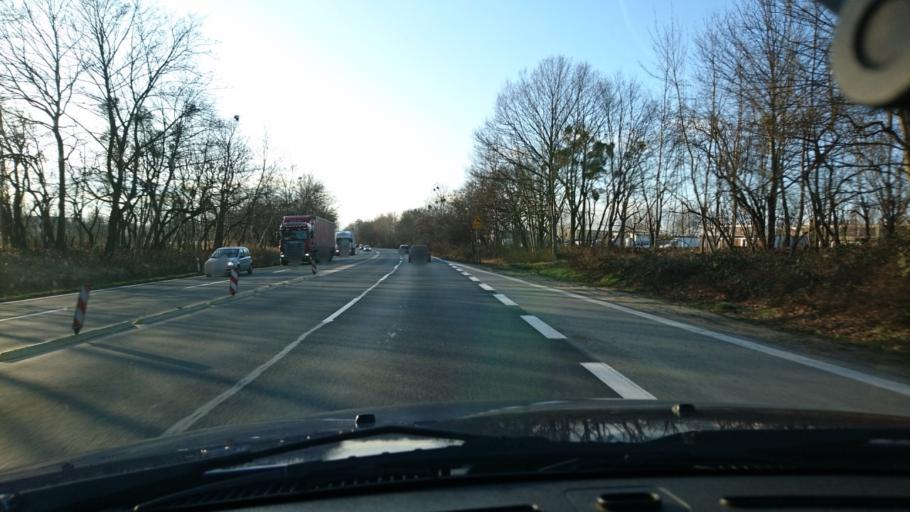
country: PL
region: Silesian Voivodeship
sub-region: Gliwice
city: Gliwice
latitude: 50.3161
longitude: 18.6876
